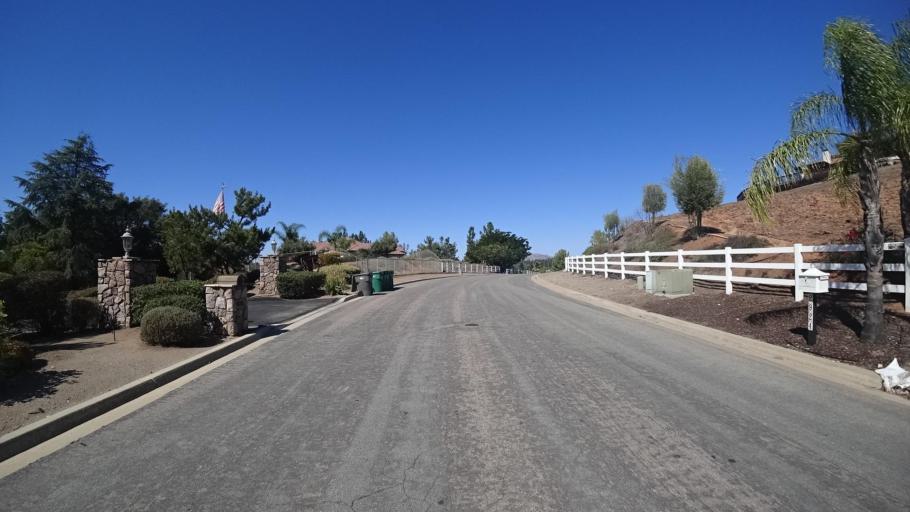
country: US
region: California
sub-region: San Diego County
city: Alpine
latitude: 32.8077
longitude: -116.7761
